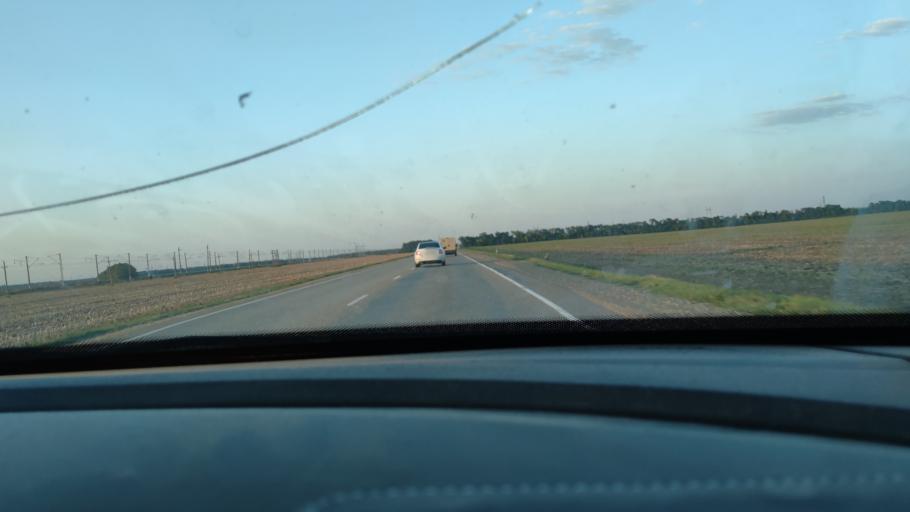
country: RU
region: Krasnodarskiy
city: Novominskaya
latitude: 46.3861
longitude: 38.9865
